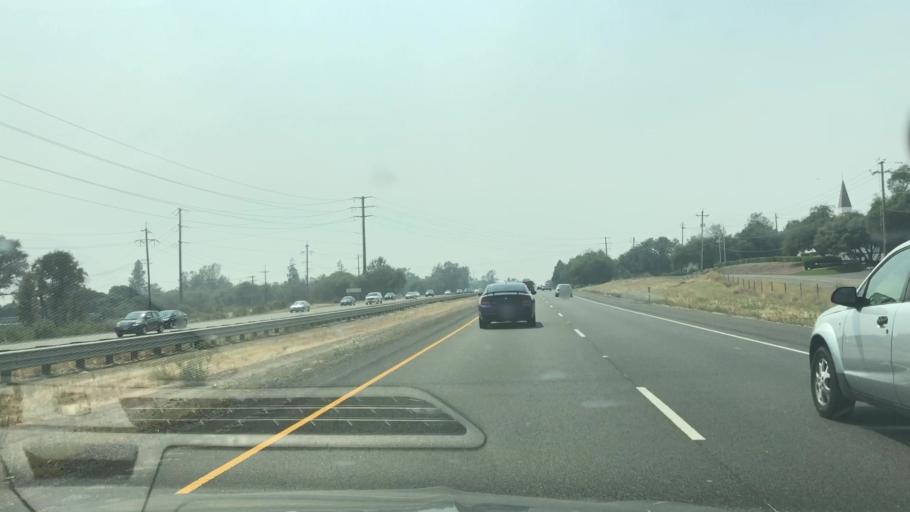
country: US
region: California
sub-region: El Dorado County
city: Shingle Springs
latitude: 38.6611
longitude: -120.9453
